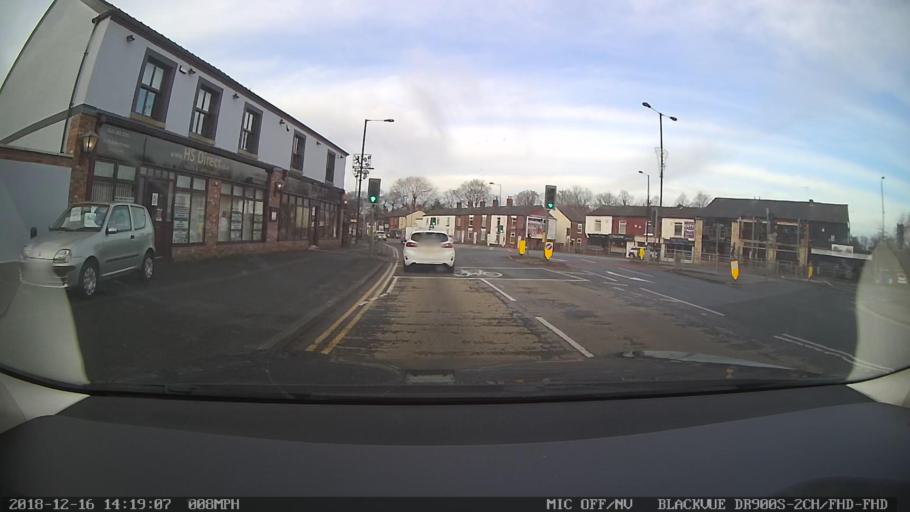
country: GB
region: England
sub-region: Borough of Stockport
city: Hazel Grove
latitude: 53.3754
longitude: -2.1139
